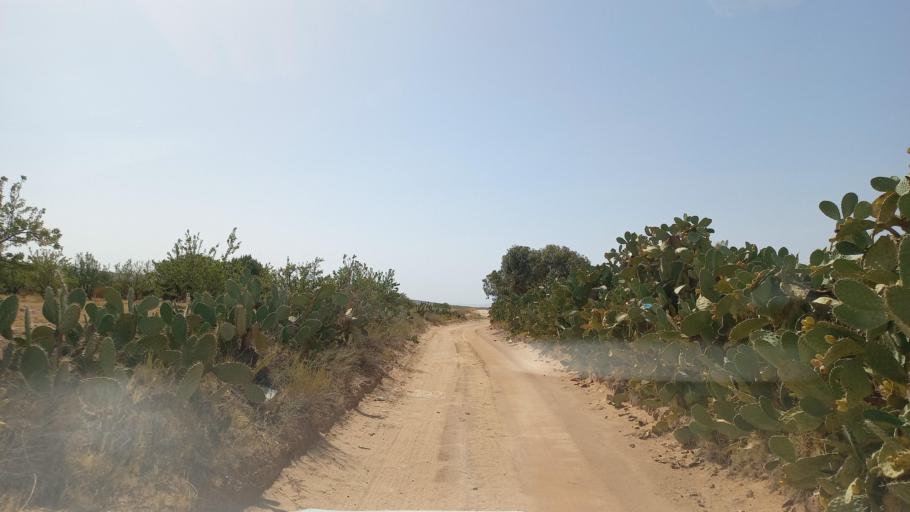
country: TN
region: Al Qasrayn
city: Kasserine
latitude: 35.2175
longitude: 9.0353
